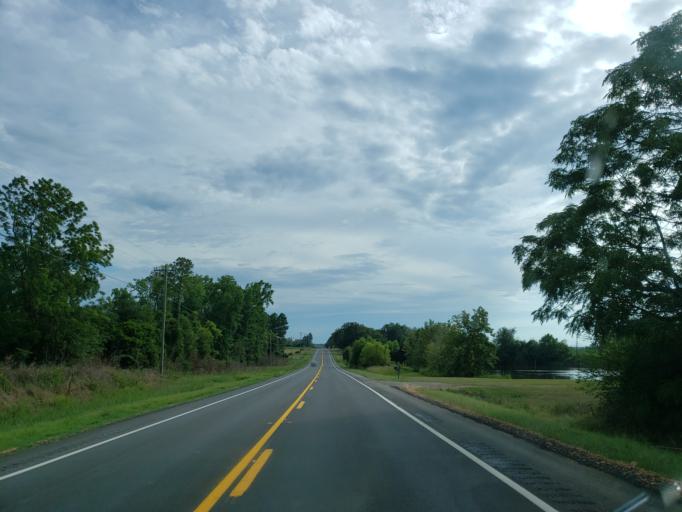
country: US
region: Georgia
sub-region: Irwin County
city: Ocilla
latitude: 31.5558
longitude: -83.3696
